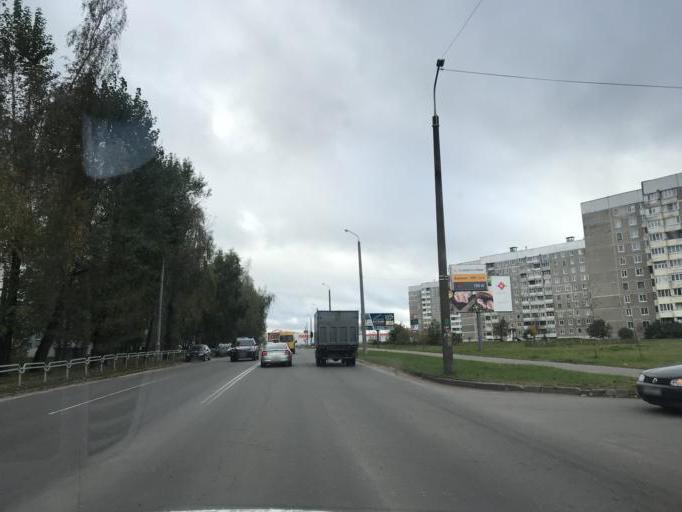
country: BY
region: Mogilev
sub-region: Mahilyowski Rayon
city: Veyno
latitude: 53.8757
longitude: 30.3663
